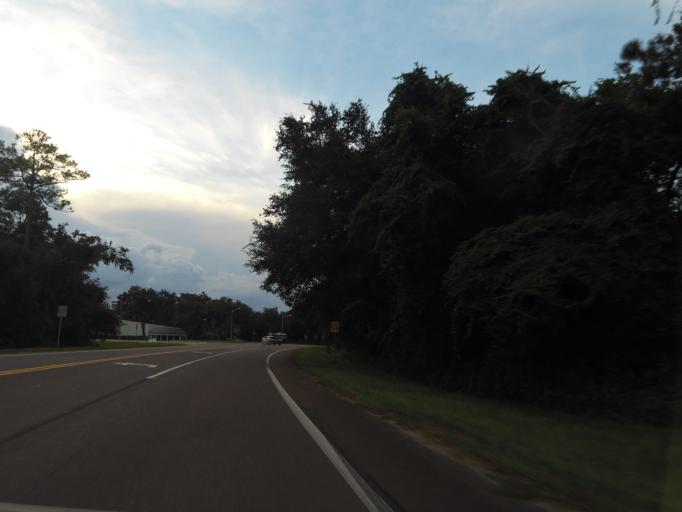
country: US
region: Florida
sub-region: Nassau County
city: Fernandina Beach
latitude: 30.6064
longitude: -81.4520
